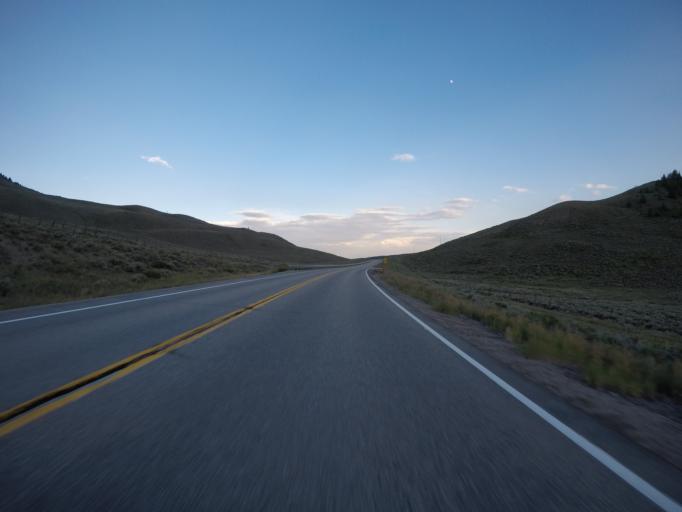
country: US
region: Colorado
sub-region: Grand County
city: Kremmling
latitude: 40.3102
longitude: -106.5106
